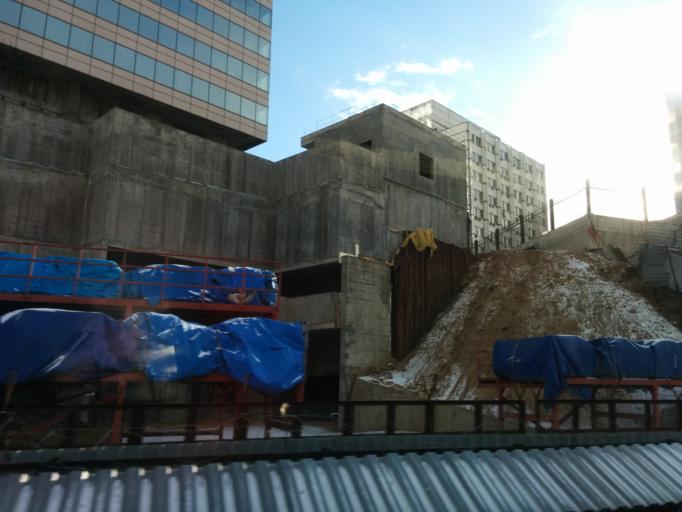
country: RU
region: Moskovskaya
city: Presnenskiy
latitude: 55.7432
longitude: 37.5304
